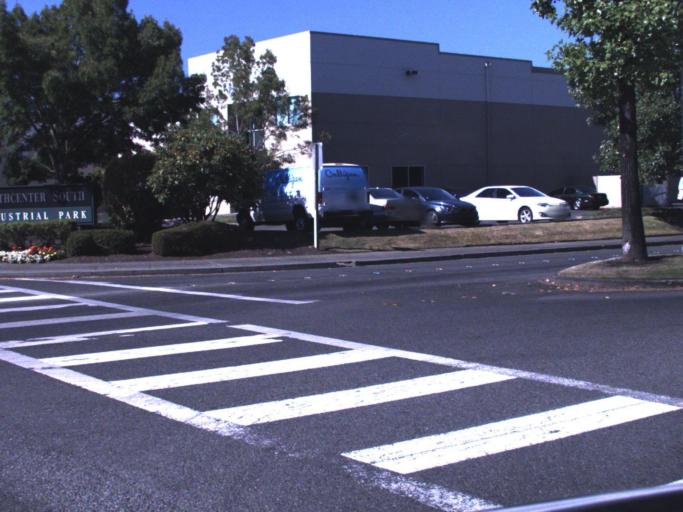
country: US
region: Washington
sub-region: King County
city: Tukwila
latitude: 47.4361
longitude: -122.2478
